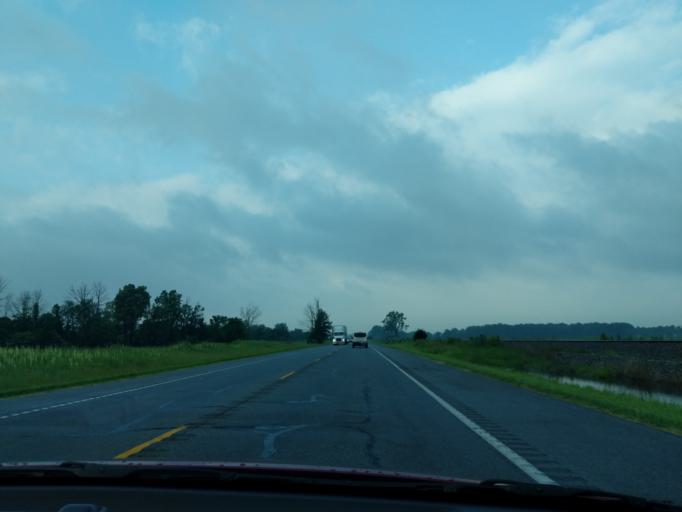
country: US
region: Indiana
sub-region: Hancock County
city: McCordsville
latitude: 39.9080
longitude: -85.8976
